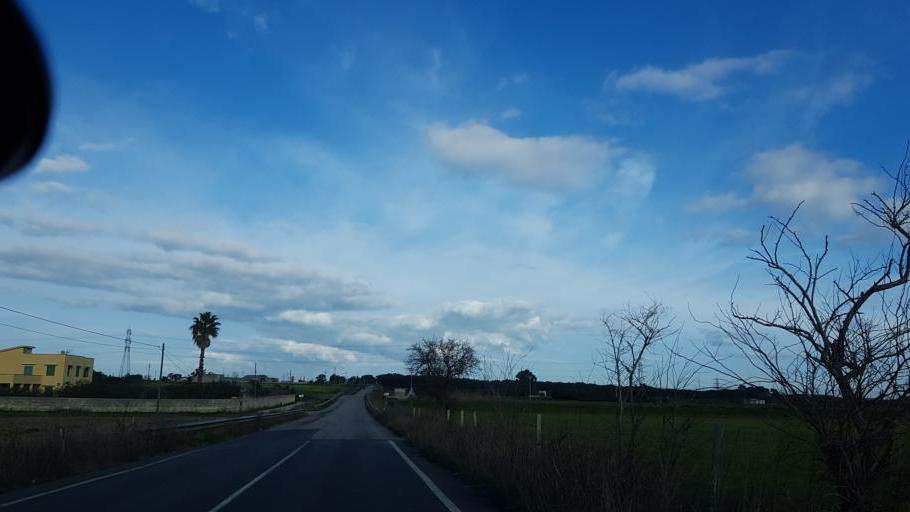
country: IT
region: Apulia
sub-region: Provincia di Brindisi
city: La Rosa
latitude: 40.5871
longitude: 17.9621
